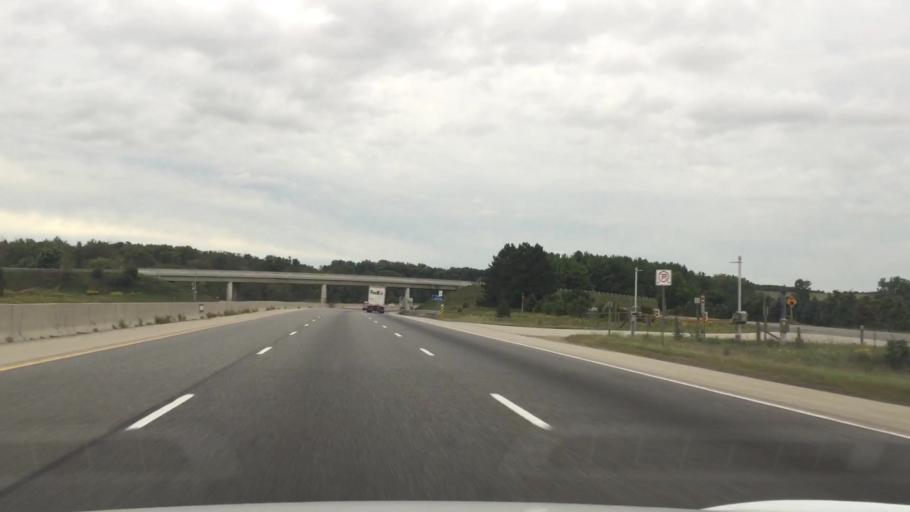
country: CA
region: Ontario
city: Kitchener
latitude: 43.3006
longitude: -80.4852
